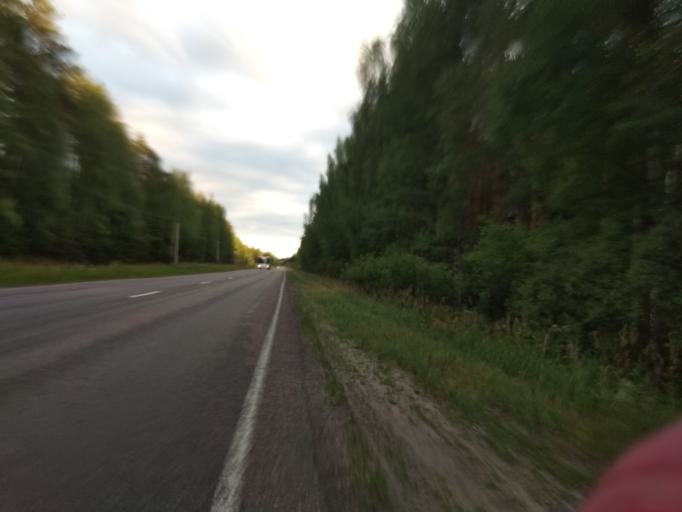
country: RU
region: Moskovskaya
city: Misheronskiy
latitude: 55.6122
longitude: 39.7184
